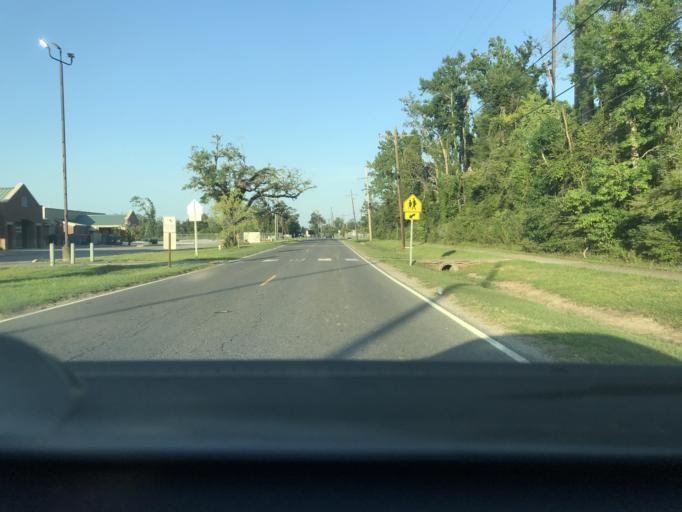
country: US
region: Louisiana
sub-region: Calcasieu Parish
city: Moss Bluff
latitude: 30.2639
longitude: -93.1918
